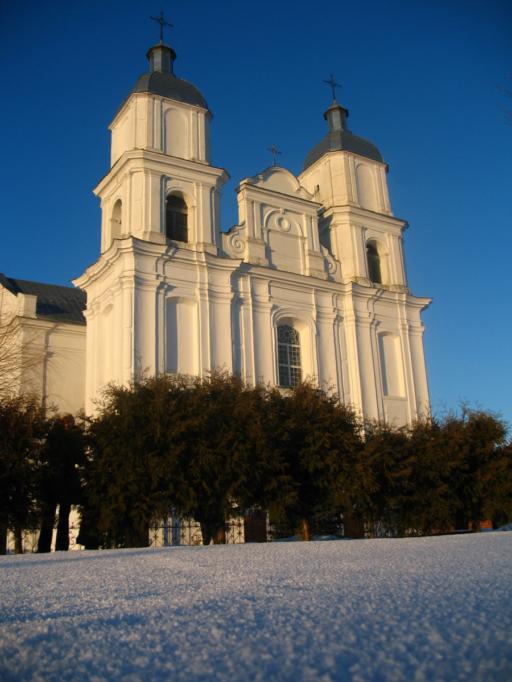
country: BY
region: Vitebsk
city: Mosar
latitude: 55.0759
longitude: 27.2351
